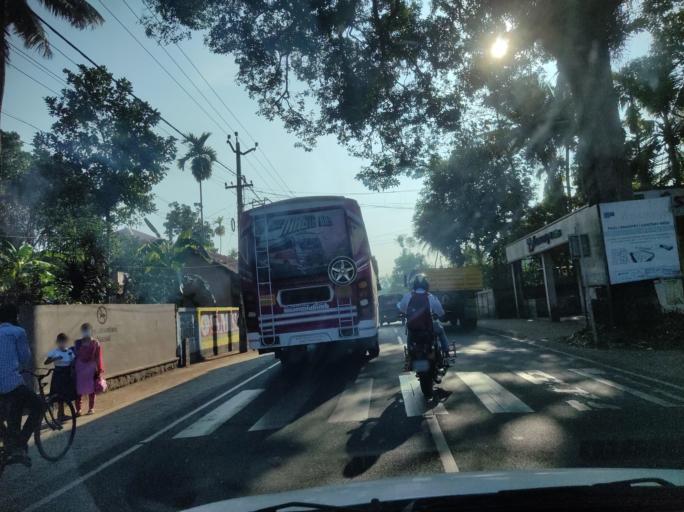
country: IN
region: Kerala
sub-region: Alappuzha
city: Kayankulam
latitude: 9.1767
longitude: 76.5232
